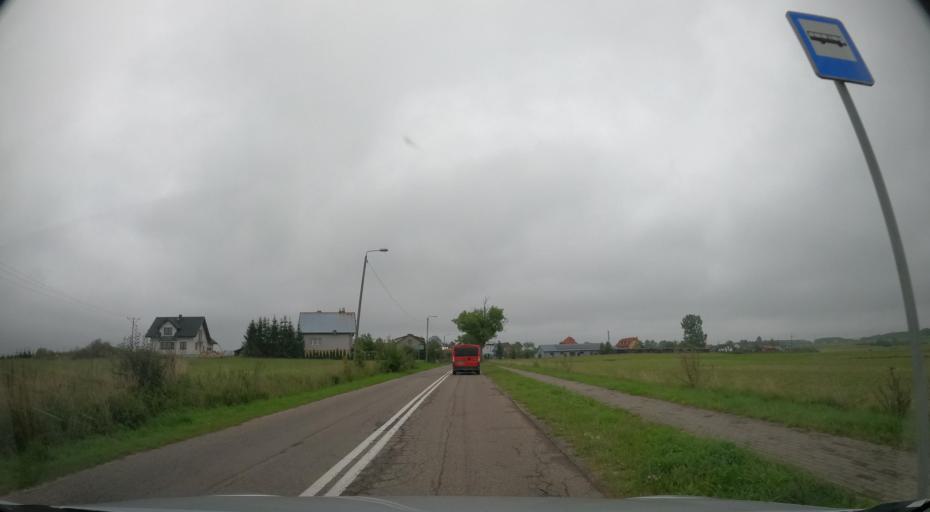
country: PL
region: Pomeranian Voivodeship
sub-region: Powiat wejherowski
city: Luzino
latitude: 54.4980
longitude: 18.1429
